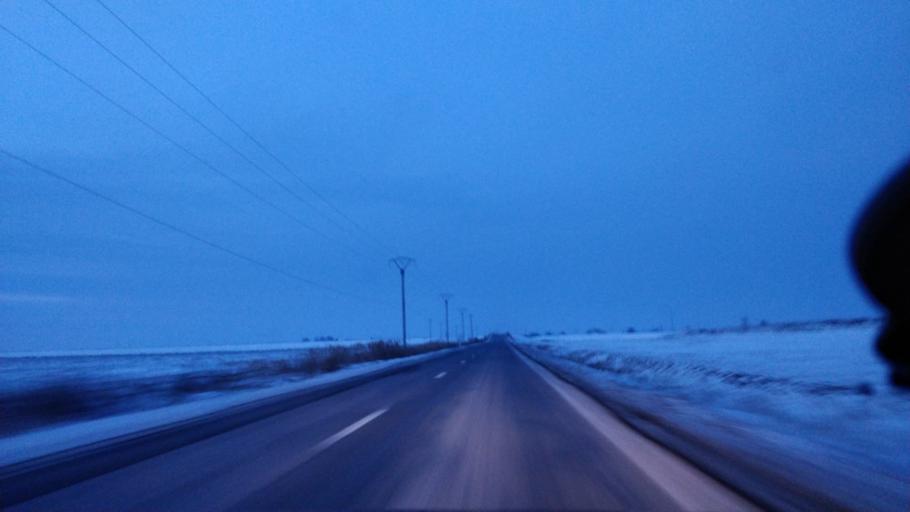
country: RO
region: Vrancea
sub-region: Comuna Nanesti
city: Nanesti
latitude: 45.5707
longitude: 27.4985
